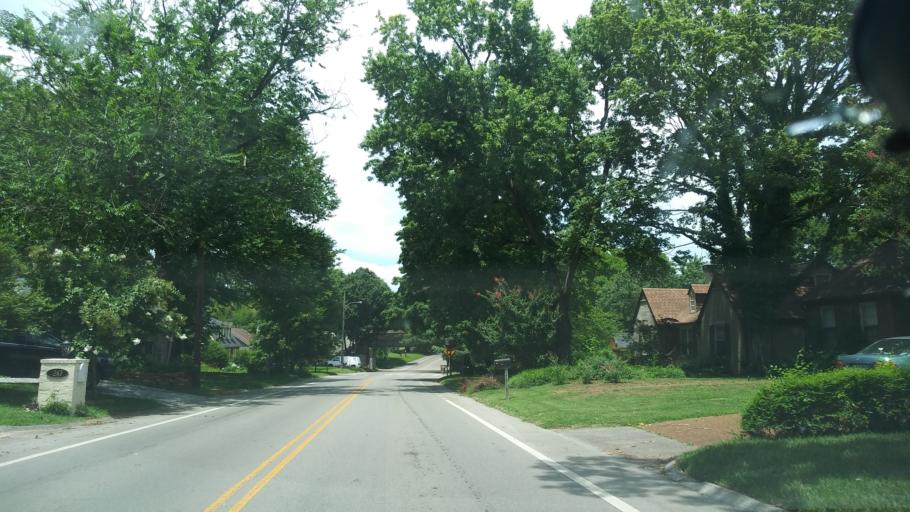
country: US
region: Tennessee
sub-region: Davidson County
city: Belle Meade
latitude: 36.1356
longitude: -86.8412
